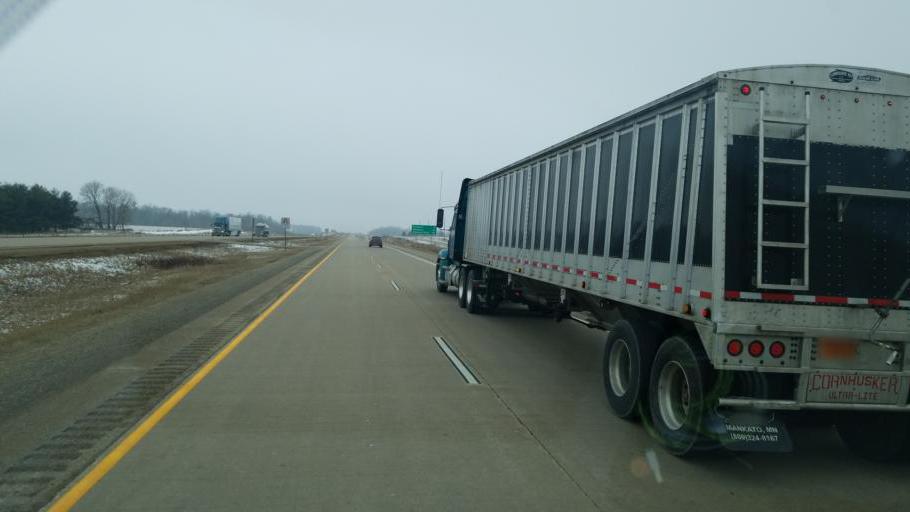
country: US
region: Wisconsin
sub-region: Winnebago County
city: Winneconne
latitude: 44.2343
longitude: -88.7522
